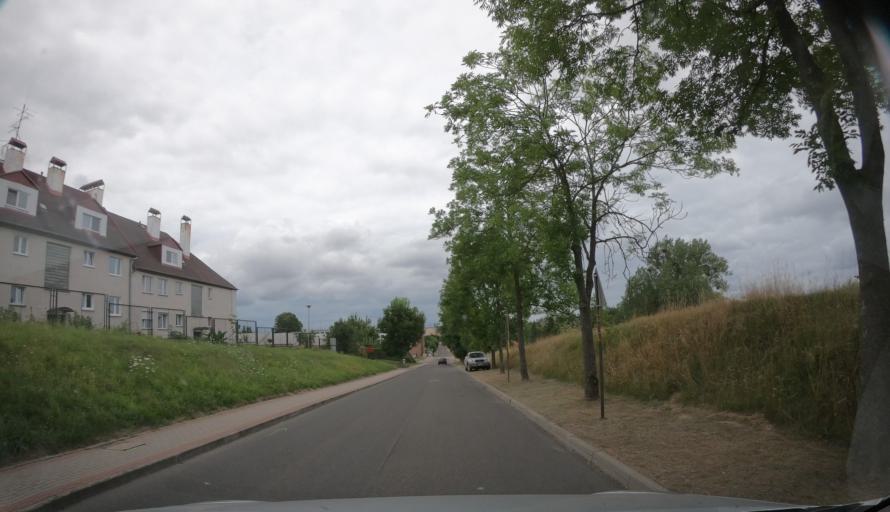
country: PL
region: West Pomeranian Voivodeship
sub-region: Powiat kamienski
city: Golczewo
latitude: 53.8207
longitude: 14.9812
